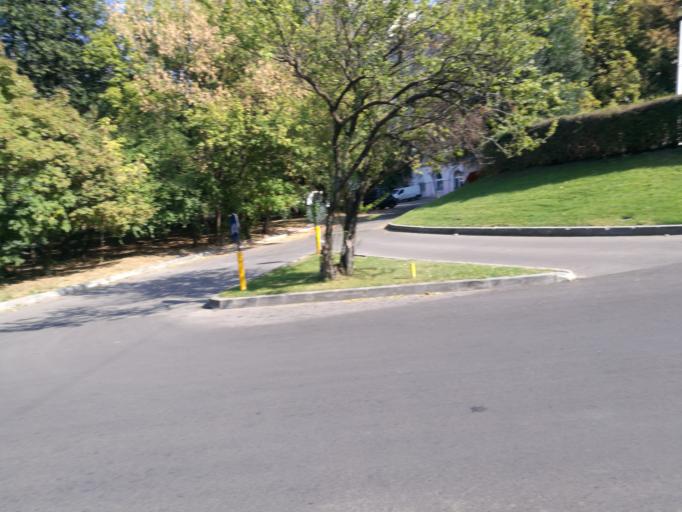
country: RO
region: Bucuresti
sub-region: Municipiul Bucuresti
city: Bucuresti
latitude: 44.4813
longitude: 26.0687
